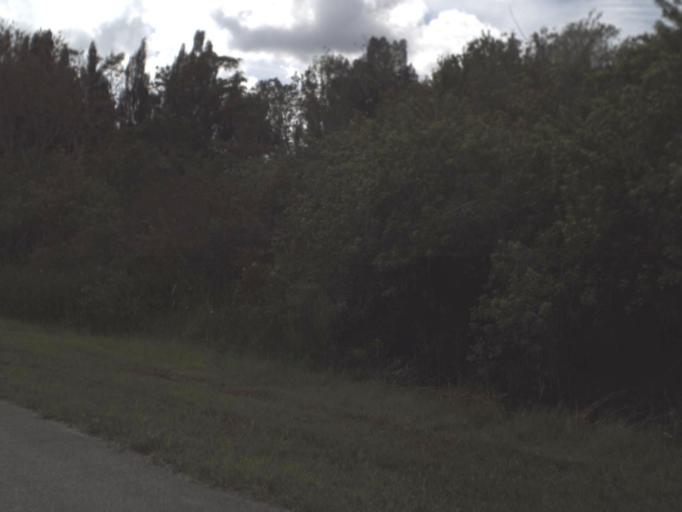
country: US
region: Florida
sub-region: Collier County
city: Lely Resort
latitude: 25.9999
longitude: -81.3469
